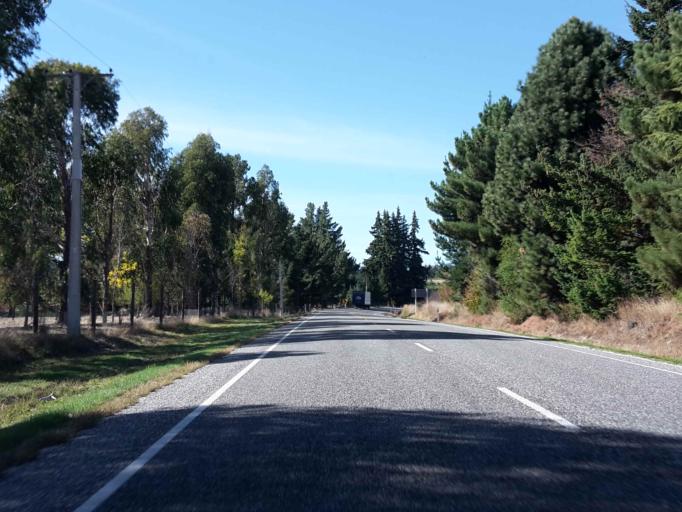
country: NZ
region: Otago
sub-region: Queenstown-Lakes District
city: Wanaka
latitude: -44.7007
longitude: 169.1896
